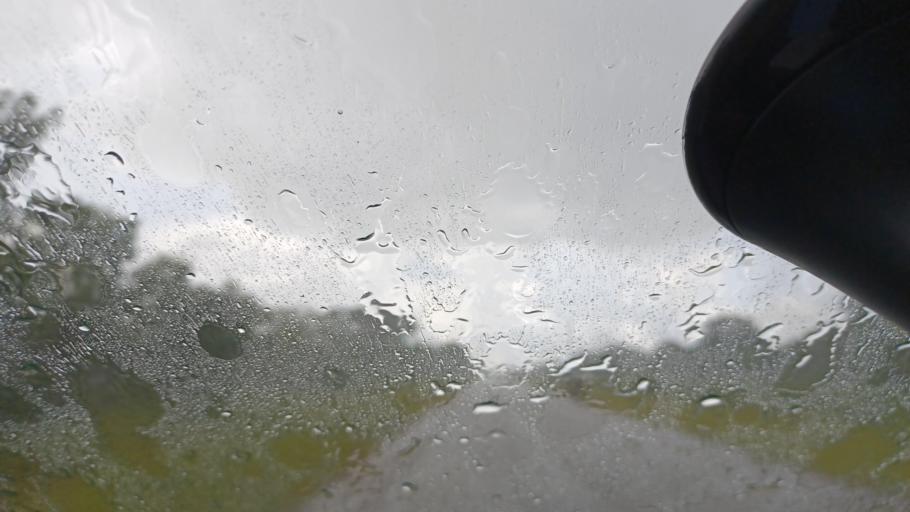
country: ZM
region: North-Western
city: Kasempa
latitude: -13.0948
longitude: 25.9155
